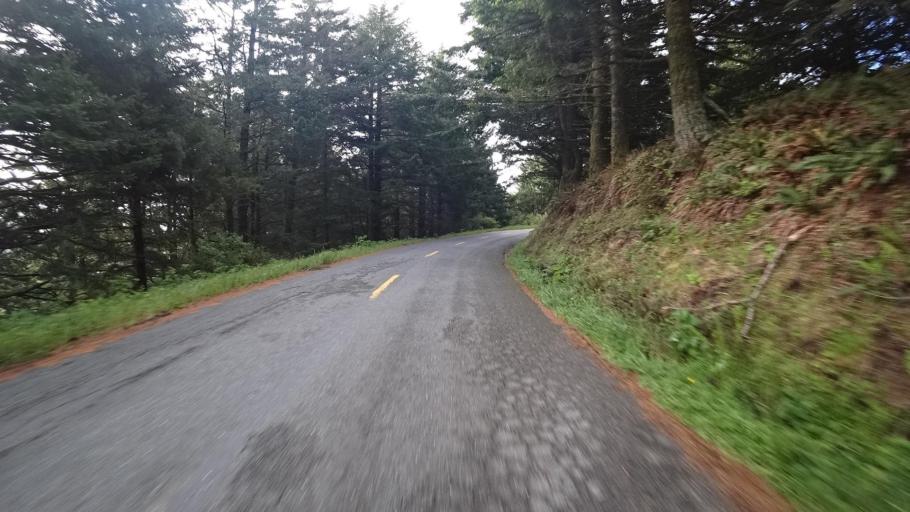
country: US
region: California
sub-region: Humboldt County
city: Ferndale
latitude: 40.4846
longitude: -124.3384
